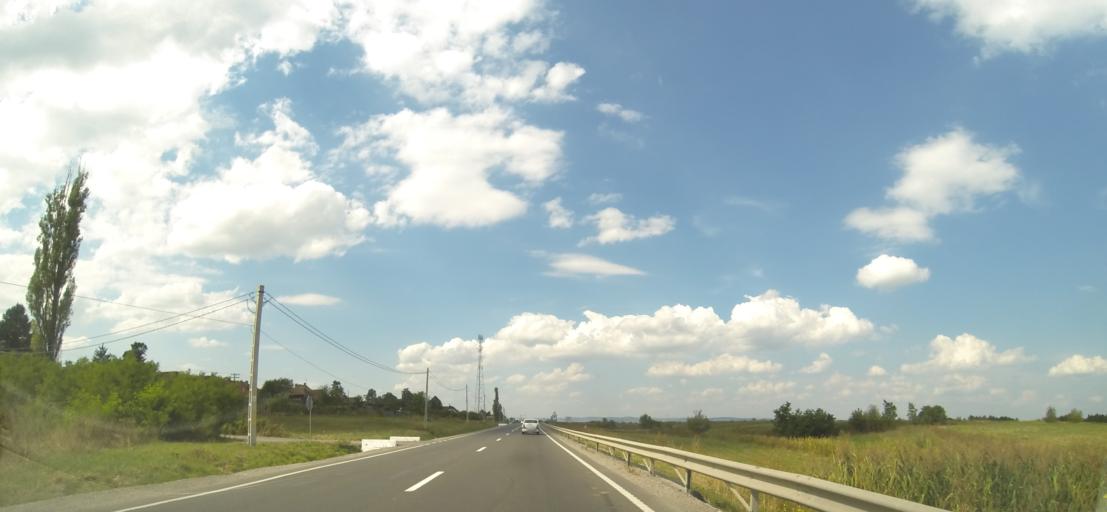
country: RO
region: Brasov
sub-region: Comuna Sinca Veche
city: Persani
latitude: 45.7870
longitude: 25.1998
